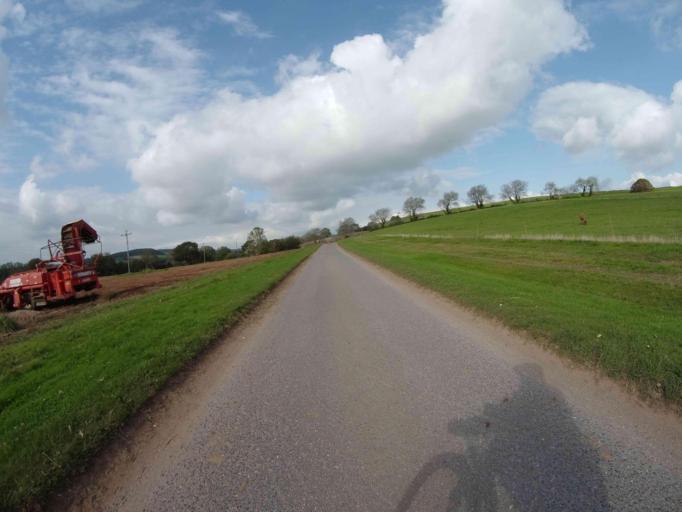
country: GB
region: England
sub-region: Devon
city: Budleigh Salterton
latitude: 50.6383
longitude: -3.3054
